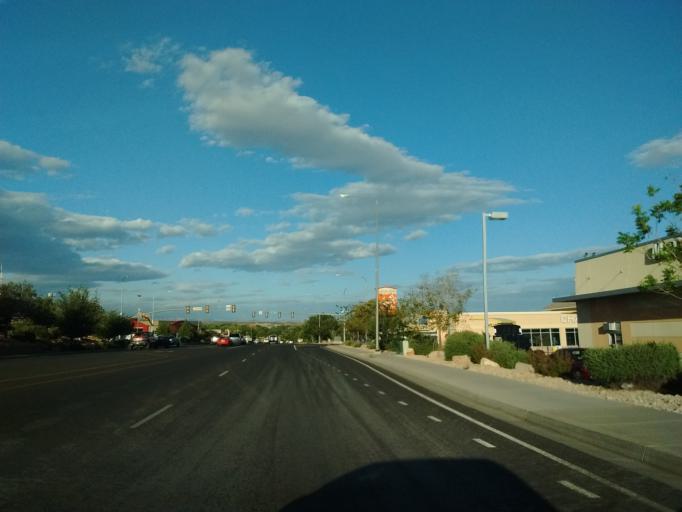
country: US
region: Utah
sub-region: Washington County
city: Washington
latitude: 37.1277
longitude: -113.5219
